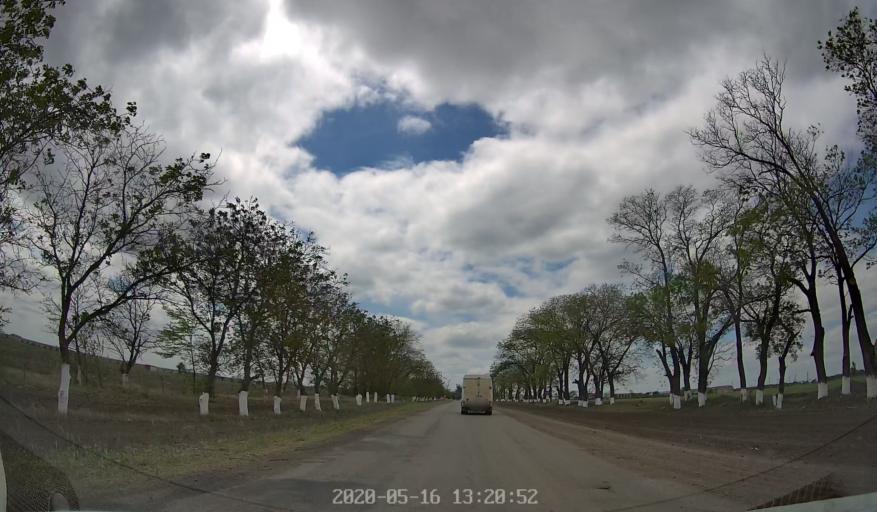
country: UA
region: Odessa
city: Lymanske
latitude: 46.5427
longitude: 30.0434
